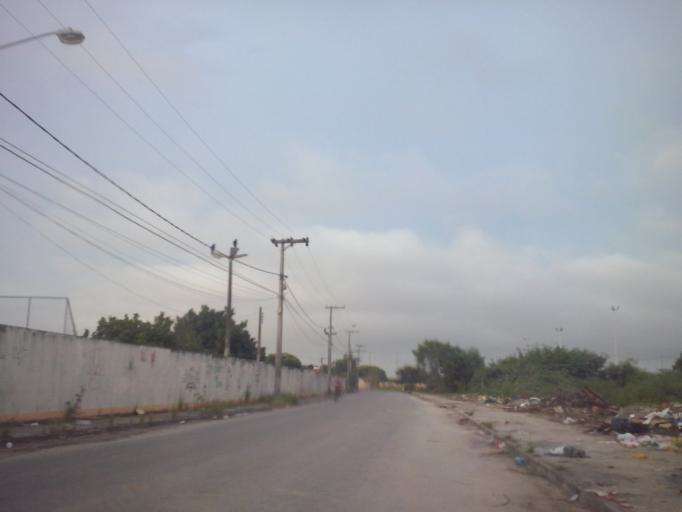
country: BR
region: Rio de Janeiro
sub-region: Rio Das Ostras
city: Rio das Ostras
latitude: -22.5331
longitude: -41.9663
